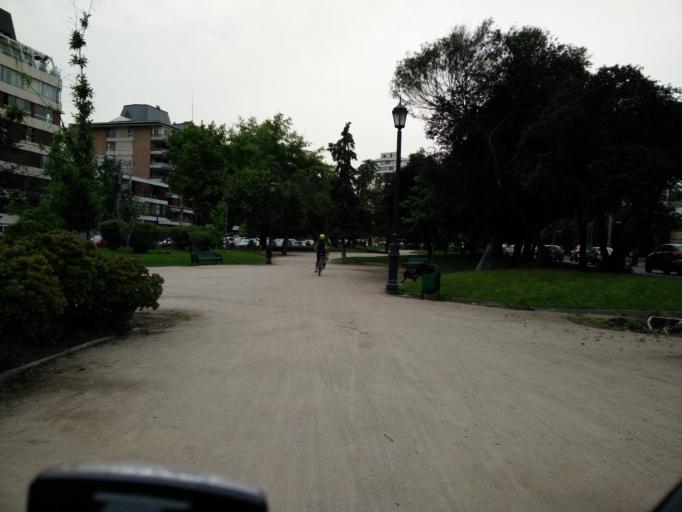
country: CL
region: Santiago Metropolitan
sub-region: Provincia de Santiago
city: Villa Presidente Frei, Nunoa, Santiago, Chile
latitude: -33.4099
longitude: -70.5867
